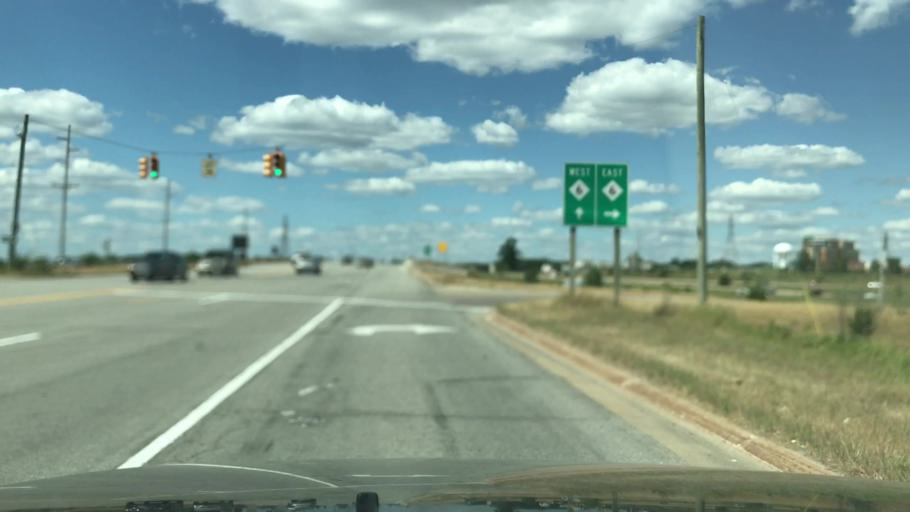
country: US
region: Michigan
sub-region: Kent County
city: Byron Center
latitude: 42.8506
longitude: -85.7228
